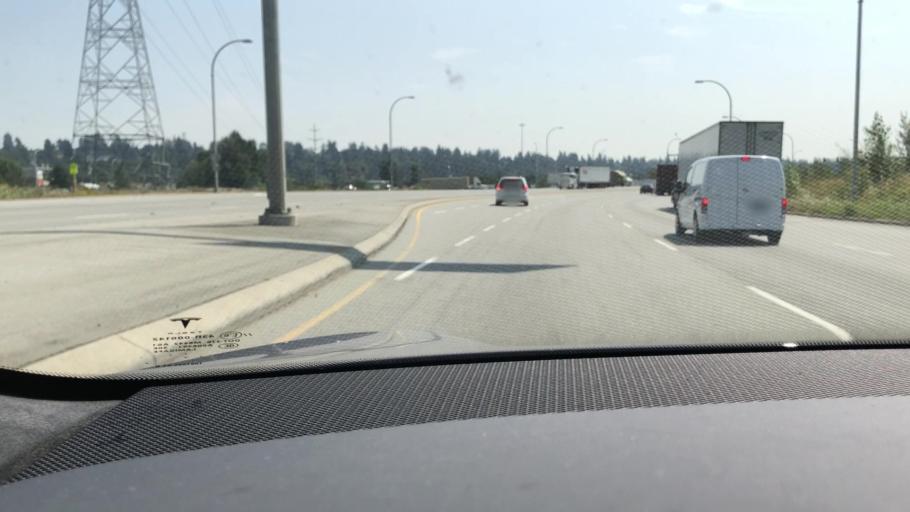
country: CA
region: British Columbia
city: Delta
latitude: 49.1464
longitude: -122.9466
